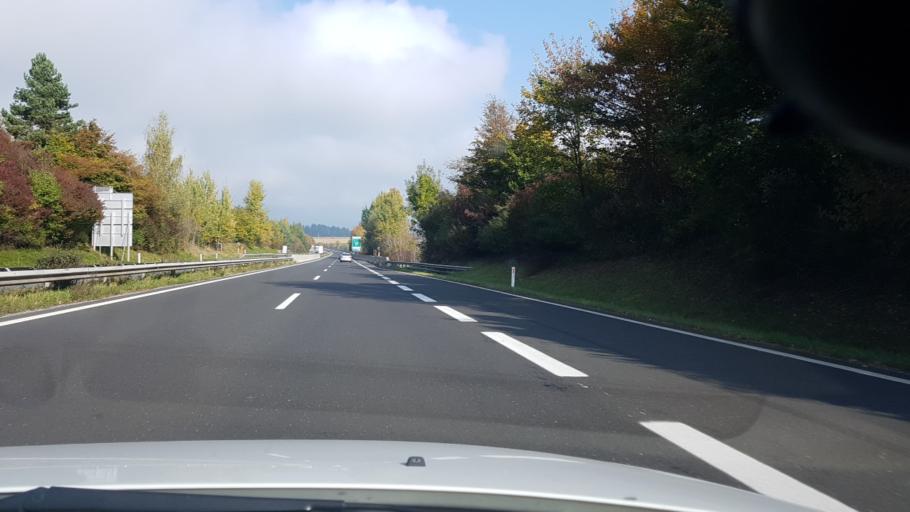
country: AT
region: Carinthia
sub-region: Politischer Bezirk Villach Land
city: Rosegg
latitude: 46.5614
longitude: 14.0063
